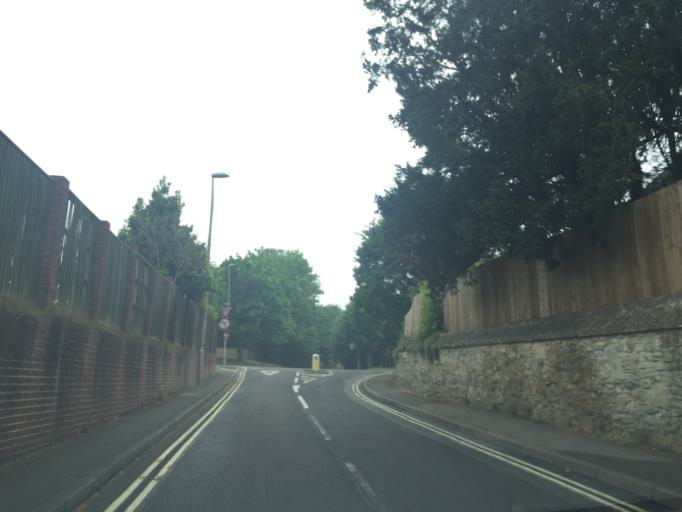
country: GB
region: England
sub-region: Dorset
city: Dorchester
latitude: 50.7103
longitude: -2.4285
